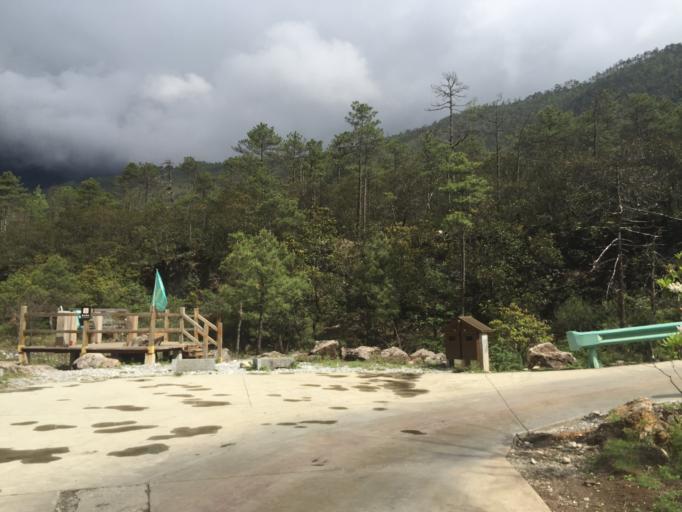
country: CN
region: Yunnan
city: Xiaqiaotou
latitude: 27.1293
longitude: 100.2359
